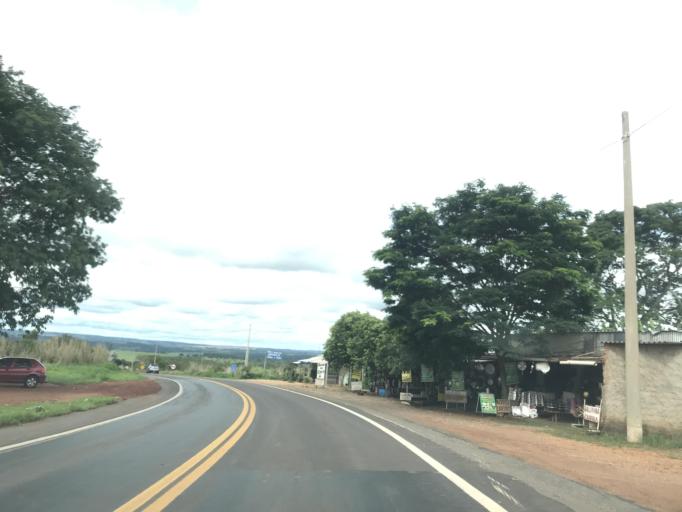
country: BR
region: Goias
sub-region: Piracanjuba
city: Piracanjuba
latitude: -17.2080
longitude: -48.7069
